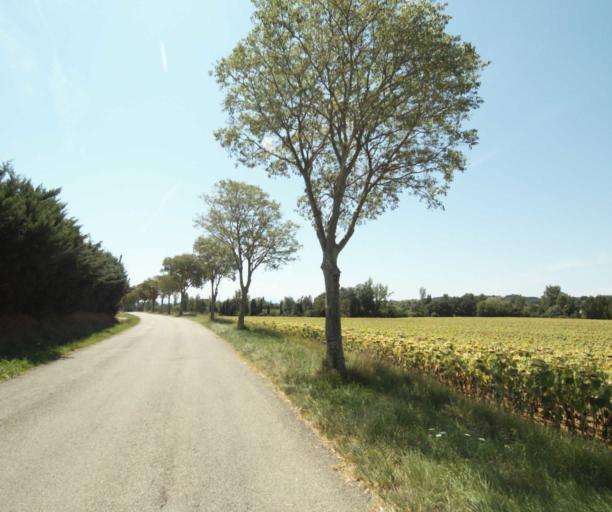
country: FR
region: Midi-Pyrenees
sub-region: Departement de l'Ariege
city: Lezat-sur-Leze
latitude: 43.2881
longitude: 1.3541
